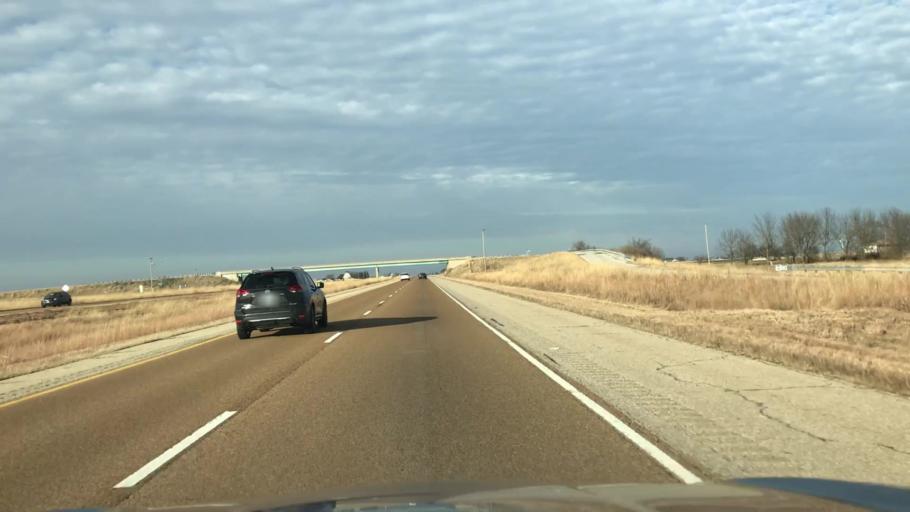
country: US
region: Illinois
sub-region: Montgomery County
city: Raymond
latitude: 39.3758
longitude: -89.6439
